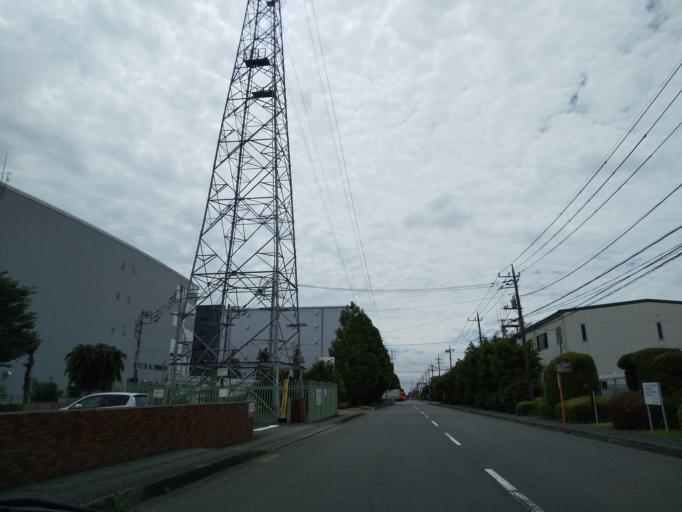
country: JP
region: Kanagawa
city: Zama
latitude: 35.5212
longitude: 139.3414
